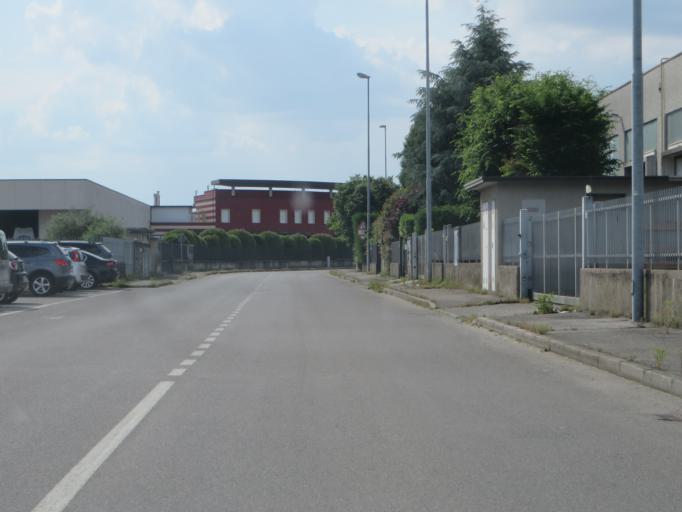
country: IT
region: Lombardy
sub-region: Provincia di Brescia
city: Cologne
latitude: 45.5698
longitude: 9.9475
